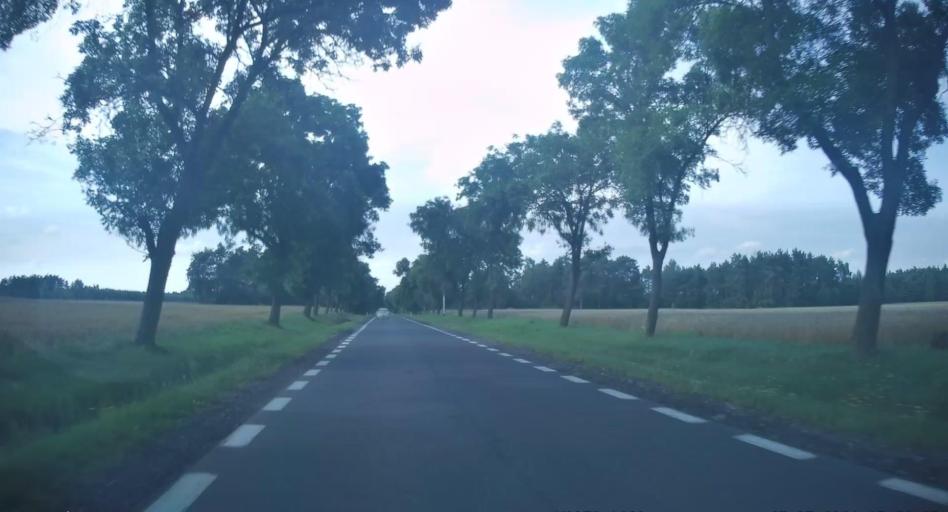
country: PL
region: Lodz Voivodeship
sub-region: Powiat tomaszowski
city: Rzeczyca
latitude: 51.6353
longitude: 20.2898
